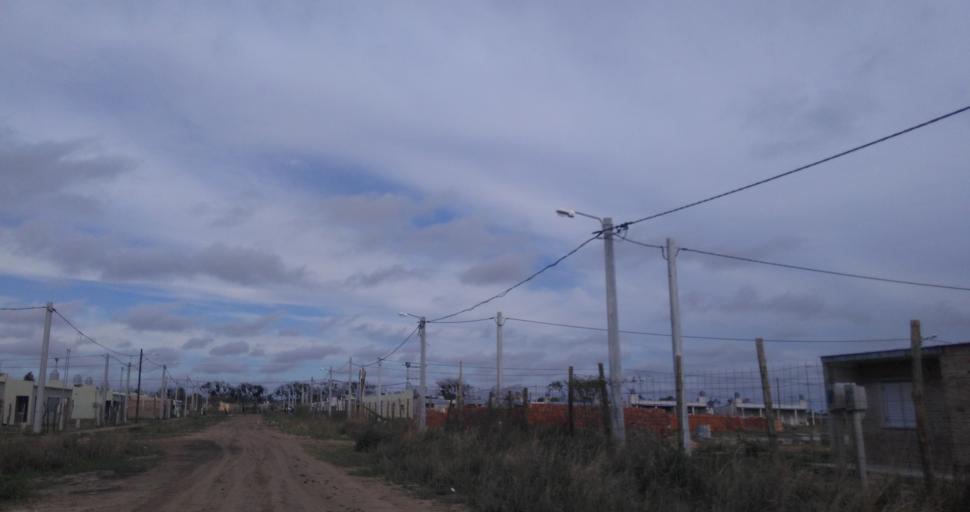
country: AR
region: Chaco
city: Fontana
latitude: -27.3950
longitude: -58.9883
